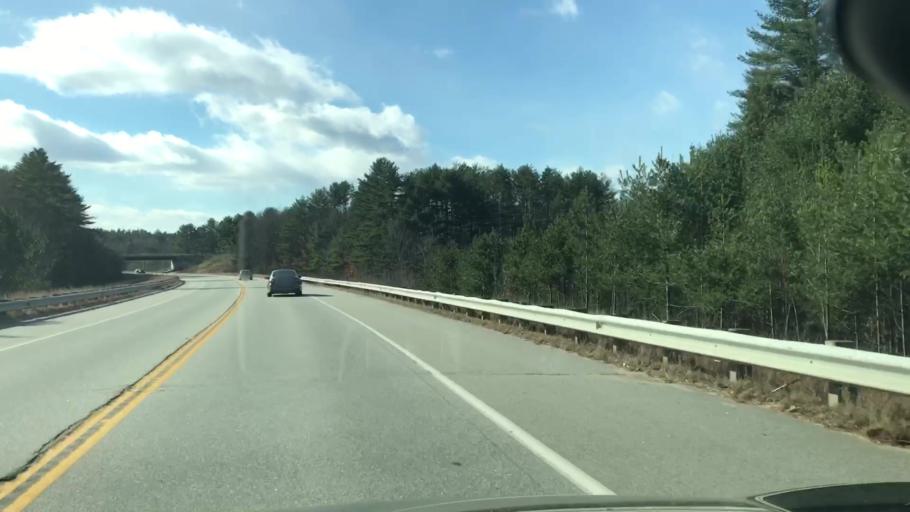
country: US
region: New Hampshire
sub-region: Belknap County
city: Barnstead
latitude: 43.3386
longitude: -71.2938
